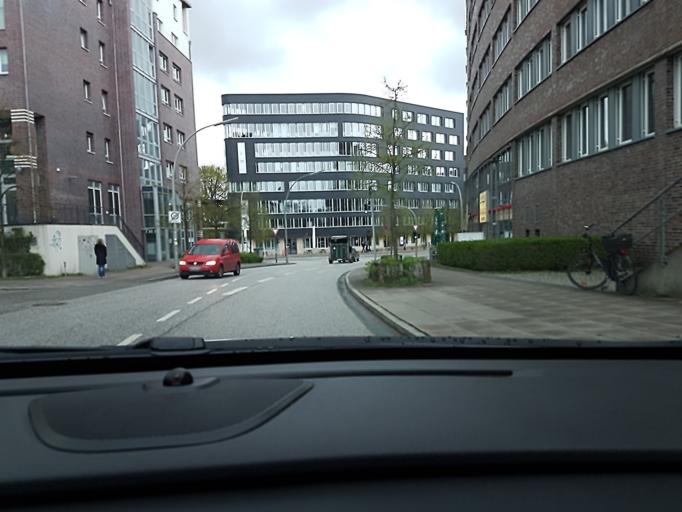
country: DE
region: Hamburg
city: Altona
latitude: 53.5592
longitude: 9.9097
